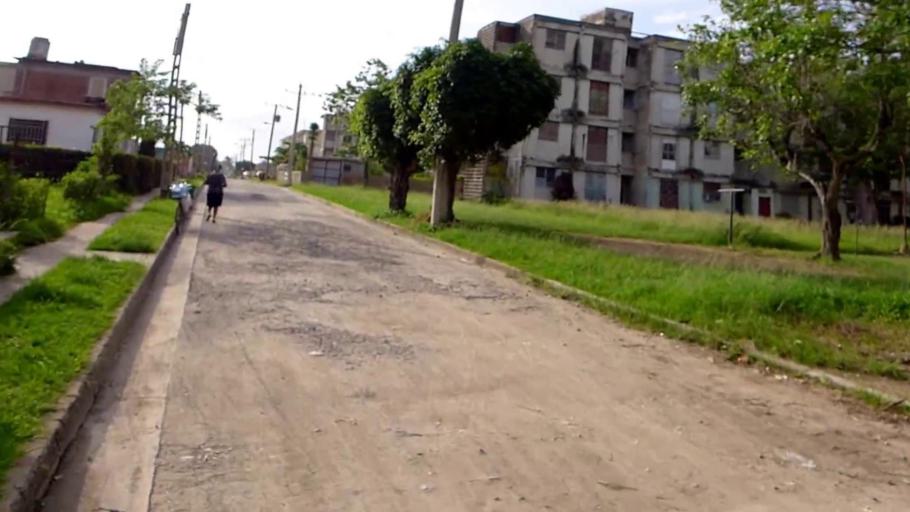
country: CU
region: Camaguey
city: Camaguey
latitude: 21.3820
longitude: -77.9385
